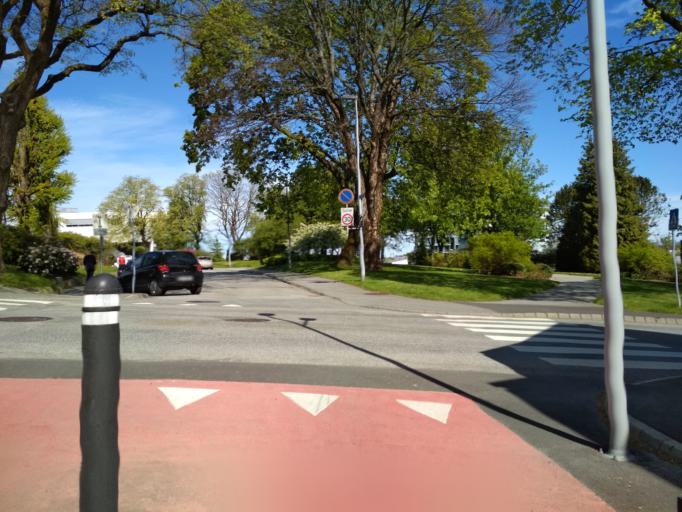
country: NO
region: Rogaland
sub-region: Stavanger
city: Stavanger
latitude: 58.9710
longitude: 5.7224
